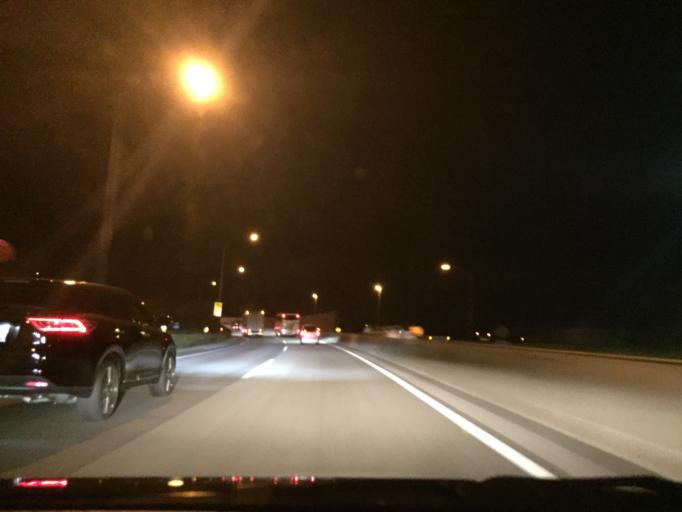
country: JP
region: Shizuoka
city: Gotemba
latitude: 35.3565
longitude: 139.0021
